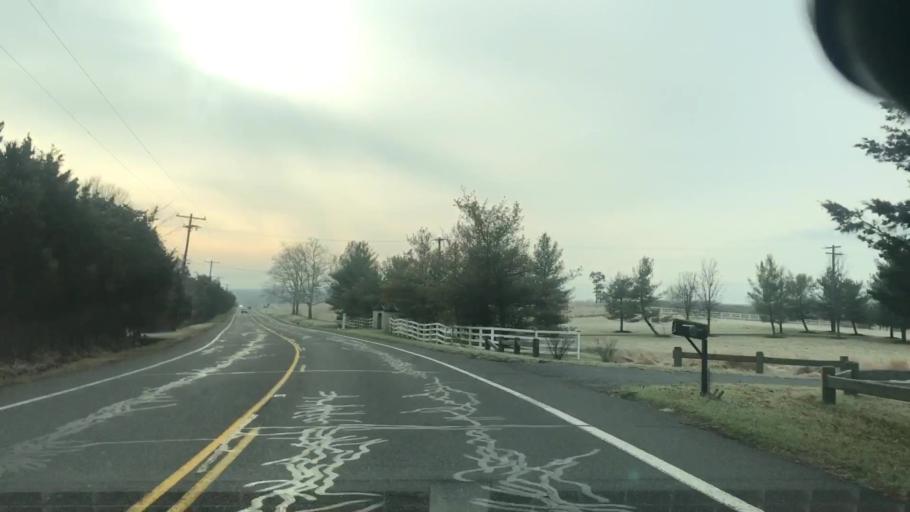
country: US
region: New Jersey
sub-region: Hunterdon County
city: Whitehouse Station
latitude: 40.6345
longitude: -74.7118
